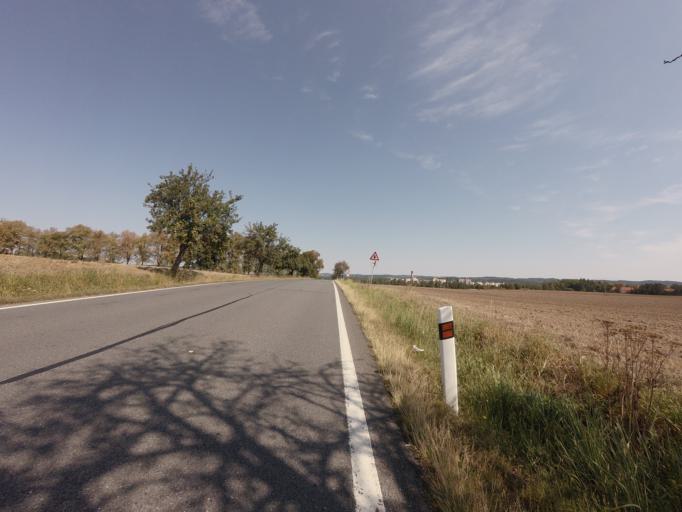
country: CZ
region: Jihocesky
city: Milevsko
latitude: 49.4369
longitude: 14.3583
